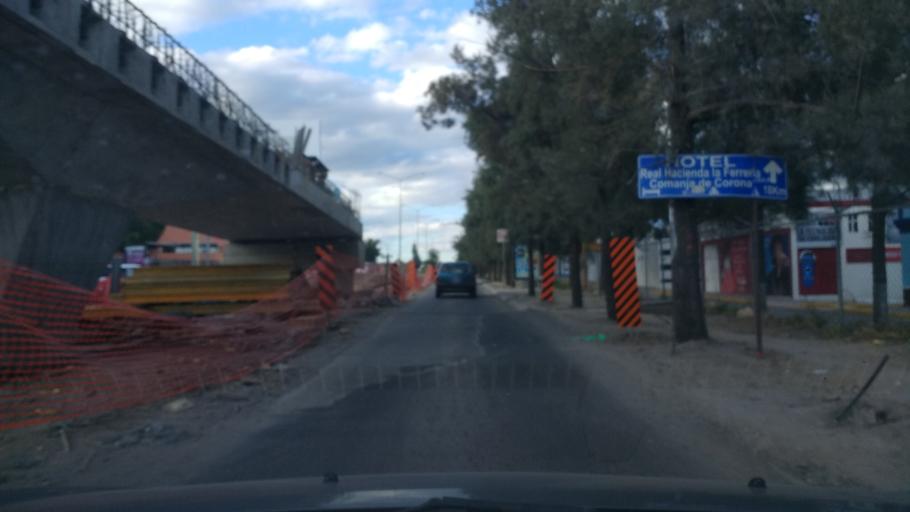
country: MX
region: Guanajuato
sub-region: Leon
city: La Ermita
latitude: 21.1710
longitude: -101.6980
